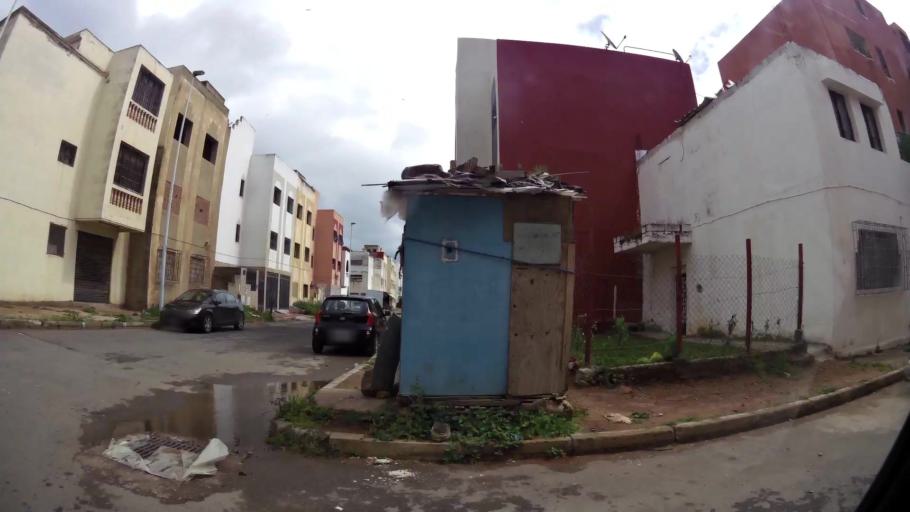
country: MA
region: Grand Casablanca
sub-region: Casablanca
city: Casablanca
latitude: 33.5663
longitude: -7.6974
